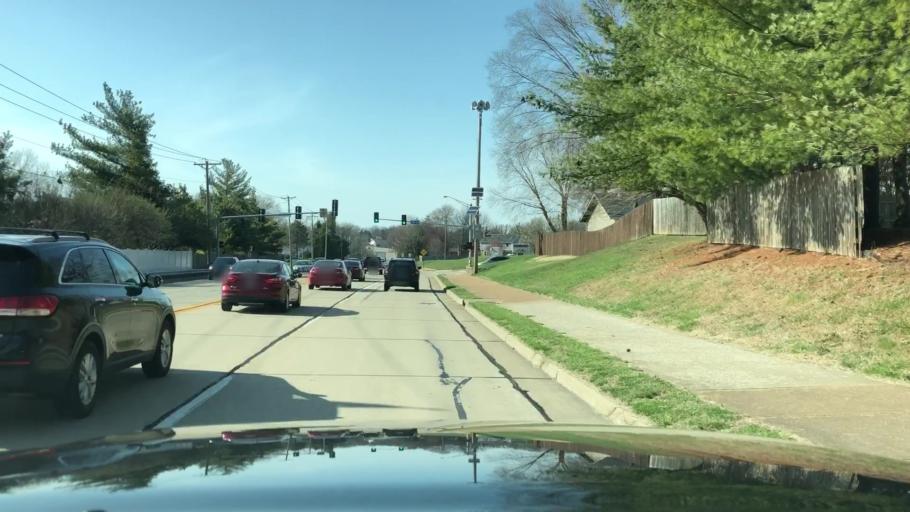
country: US
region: Missouri
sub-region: Saint Charles County
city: Saint Charles
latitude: 38.7762
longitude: -90.5528
